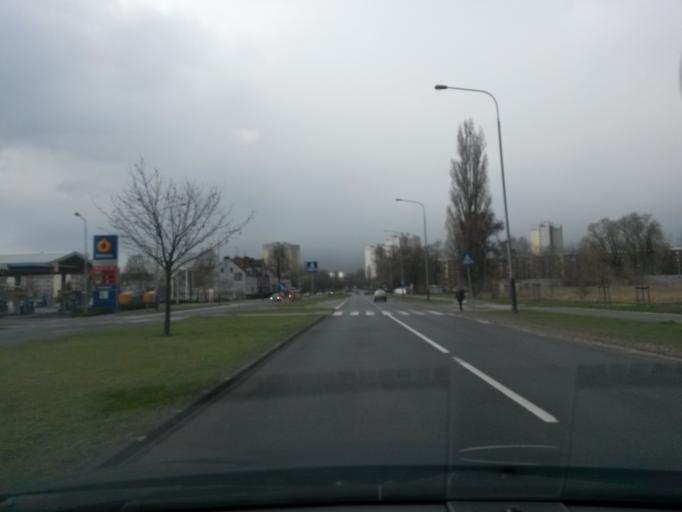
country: PL
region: Greater Poland Voivodeship
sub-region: Poznan
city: Poznan
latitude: 52.3861
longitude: 16.9623
